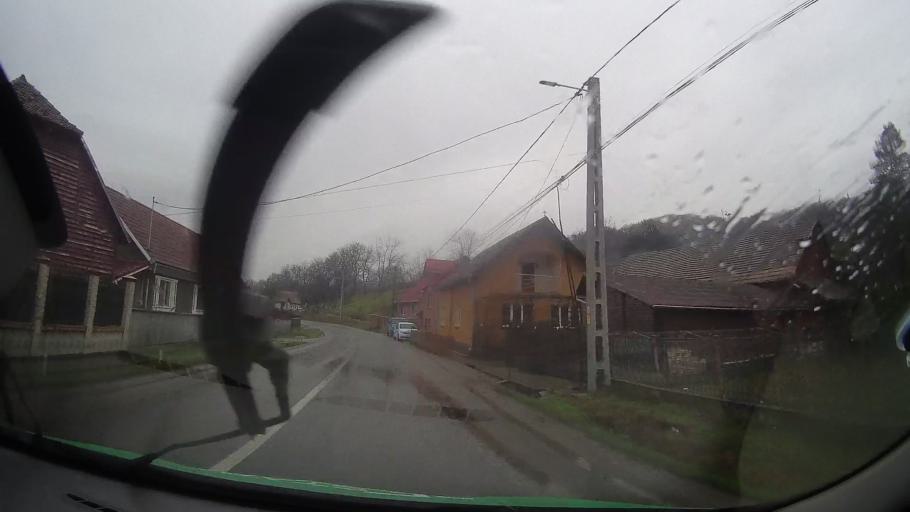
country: RO
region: Bistrita-Nasaud
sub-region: Comuna Sieut
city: Sieut
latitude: 46.9777
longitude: 24.6451
